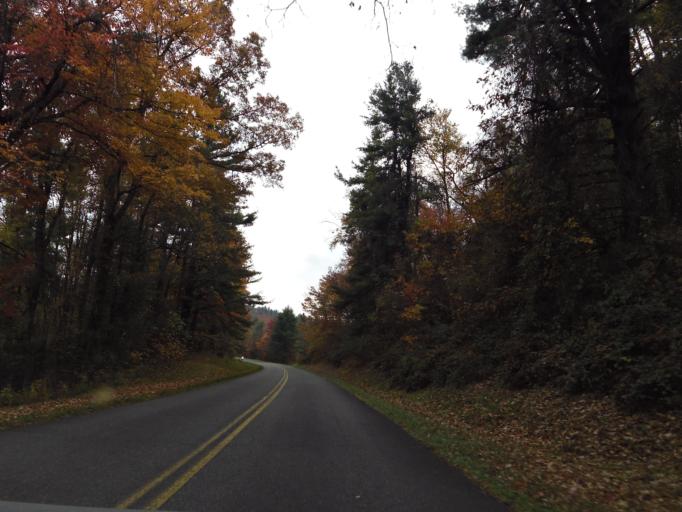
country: US
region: North Carolina
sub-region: Ashe County
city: West Jefferson
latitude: 36.2729
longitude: -81.4290
